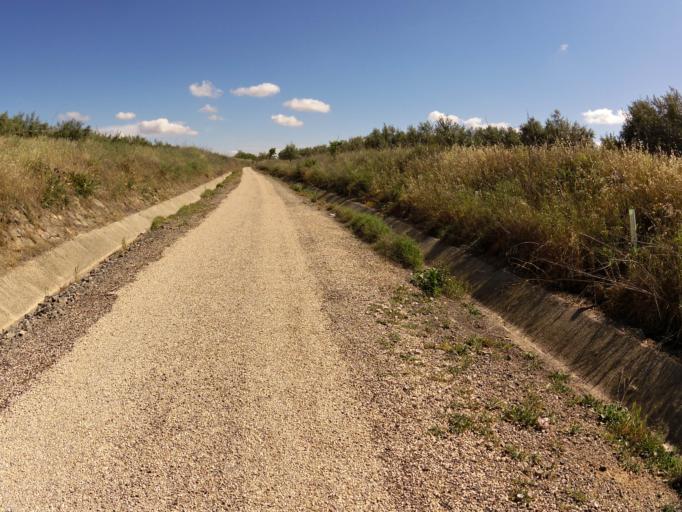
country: ES
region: Andalusia
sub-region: Provincia de Jaen
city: Alcaudete
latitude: 37.6053
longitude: -4.1298
